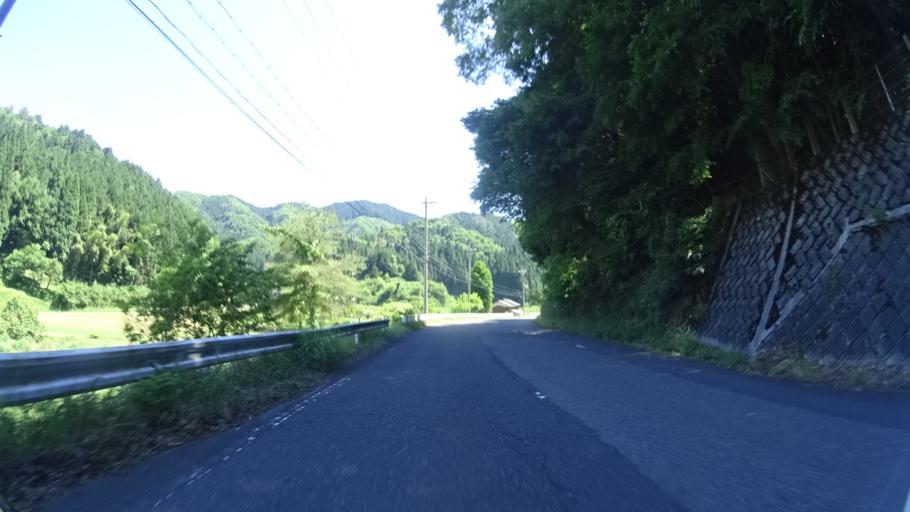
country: JP
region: Kyoto
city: Fukuchiyama
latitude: 35.4182
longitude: 135.0676
